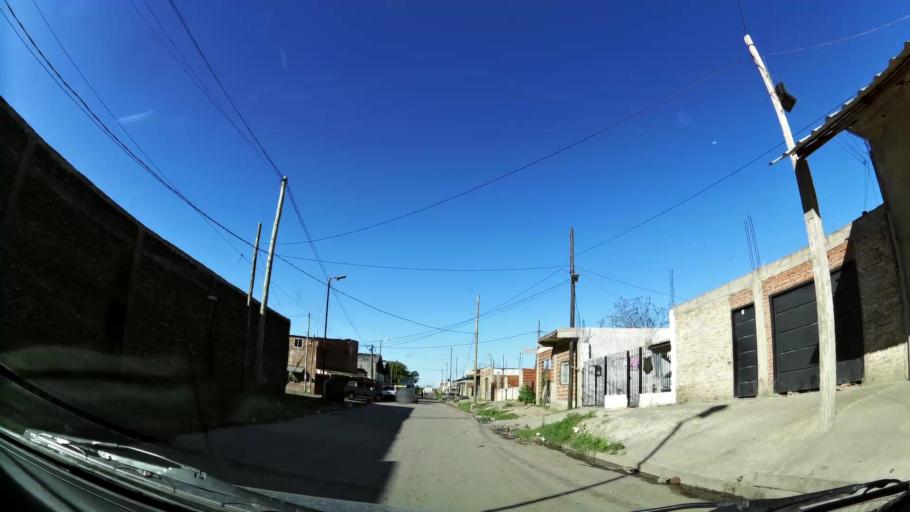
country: AR
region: Buenos Aires
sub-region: Partido de Quilmes
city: Quilmes
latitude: -34.7480
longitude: -58.3128
